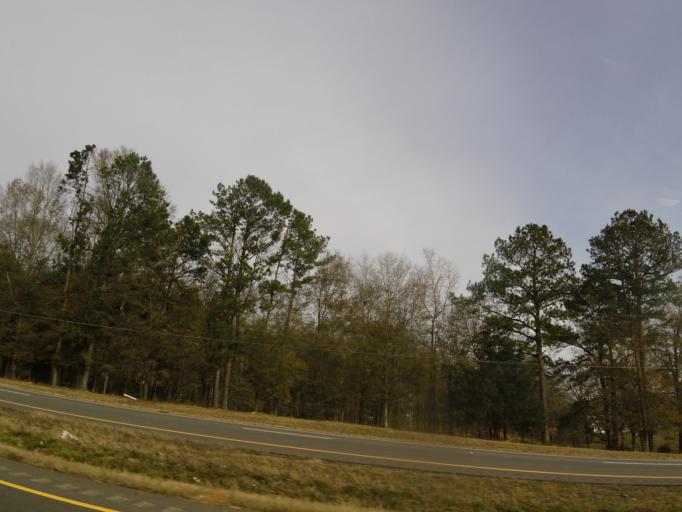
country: US
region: Alabama
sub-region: Dale County
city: Ozark
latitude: 31.5159
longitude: -85.7082
